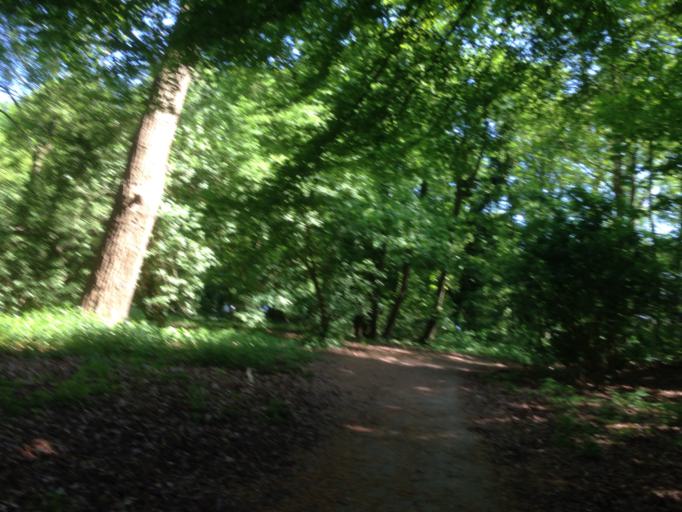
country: NL
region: Gelderland
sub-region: Gemeente Overbetuwe
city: Randwijk
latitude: 51.9655
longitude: 5.6928
